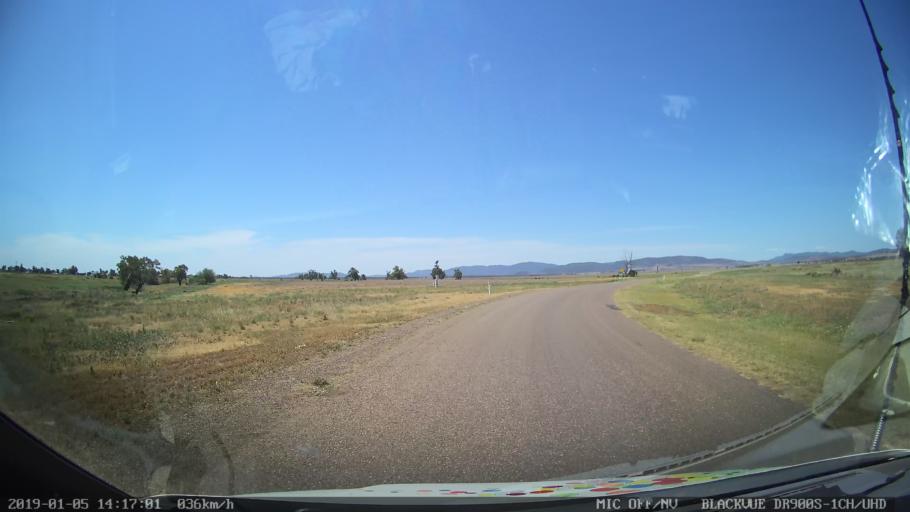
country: AU
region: New South Wales
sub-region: Liverpool Plains
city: Quirindi
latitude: -31.2557
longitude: 150.4740
